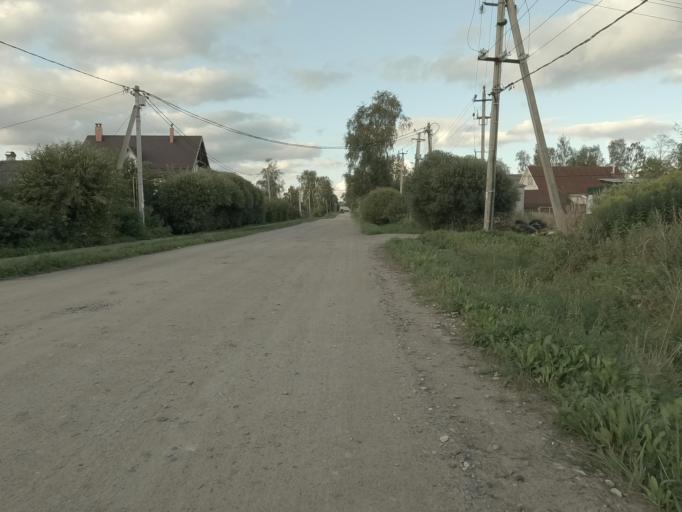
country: RU
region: Leningrad
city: Mga
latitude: 59.7518
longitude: 31.0513
